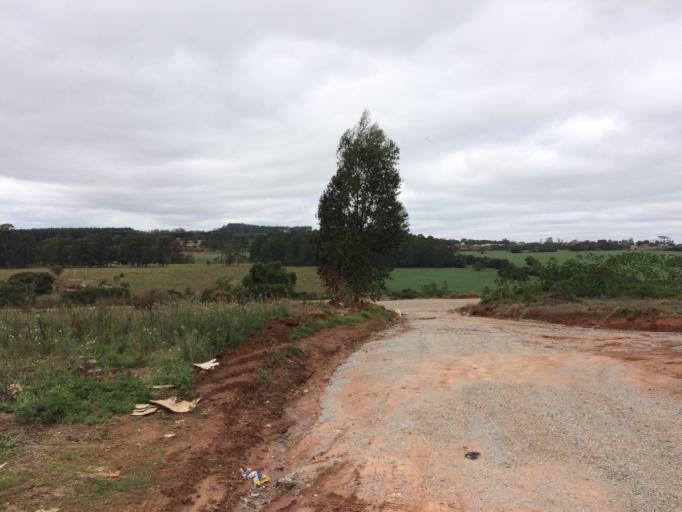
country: BR
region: Sao Paulo
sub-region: Buri
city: Buri
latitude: -23.8052
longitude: -48.6057
